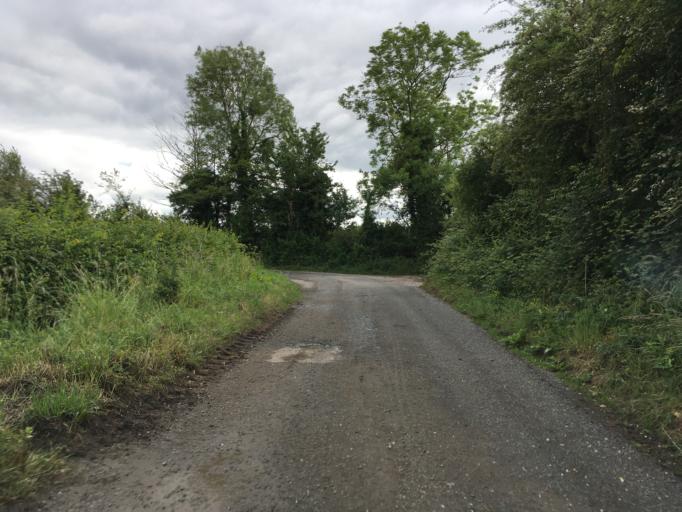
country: GB
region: England
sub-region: Gloucestershire
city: Cinderford
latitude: 51.8028
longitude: -2.4212
